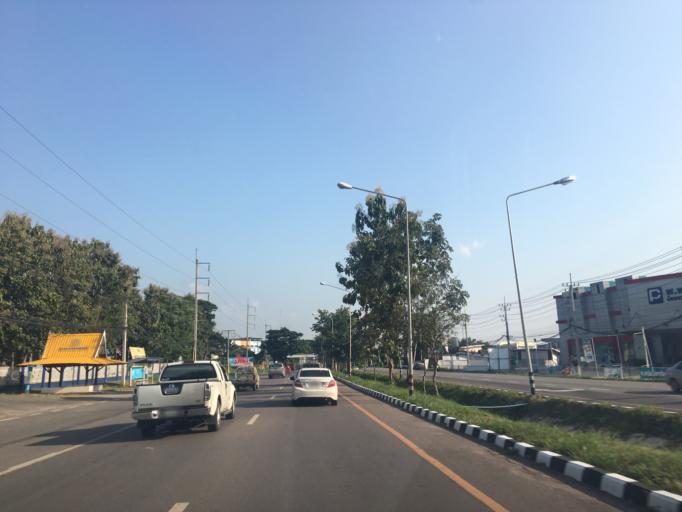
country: TH
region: Phayao
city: Phayao
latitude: 19.1663
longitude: 99.9106
